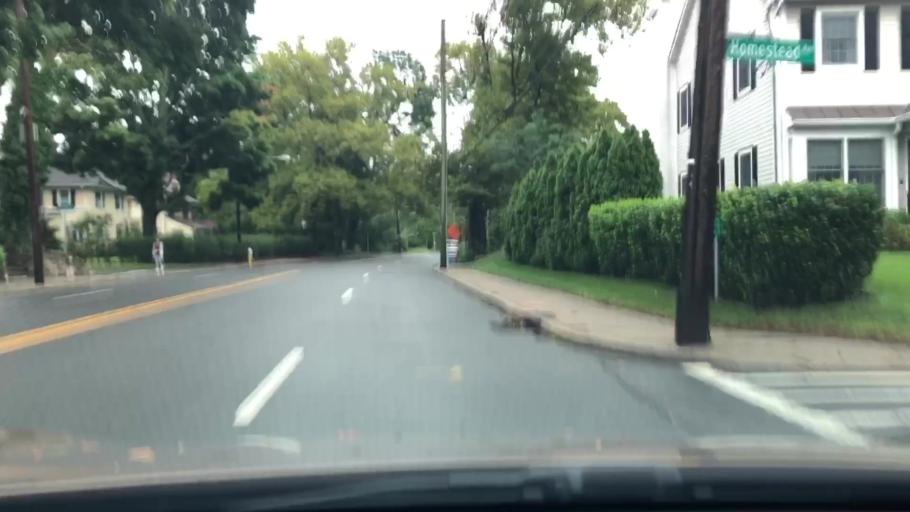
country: US
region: New York
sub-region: Westchester County
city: Greenville
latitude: 40.9780
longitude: -73.8020
